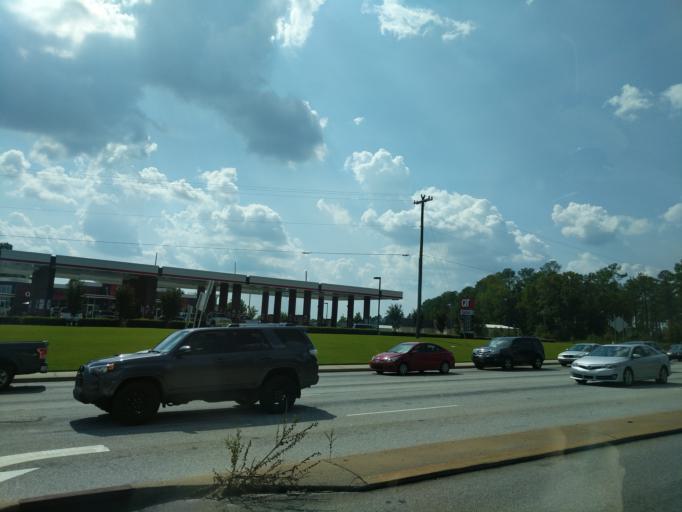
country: US
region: South Carolina
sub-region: Greenville County
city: Greer
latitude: 34.8768
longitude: -82.2262
